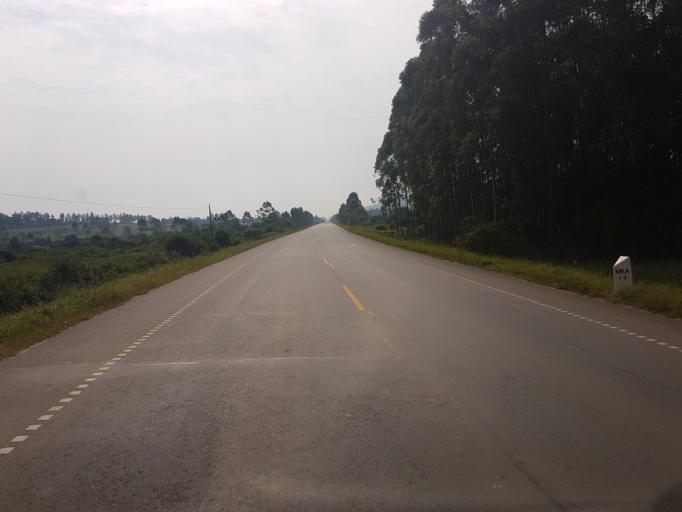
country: UG
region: Western Region
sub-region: Sheema District
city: Kibingo
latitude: -0.6481
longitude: 30.4882
